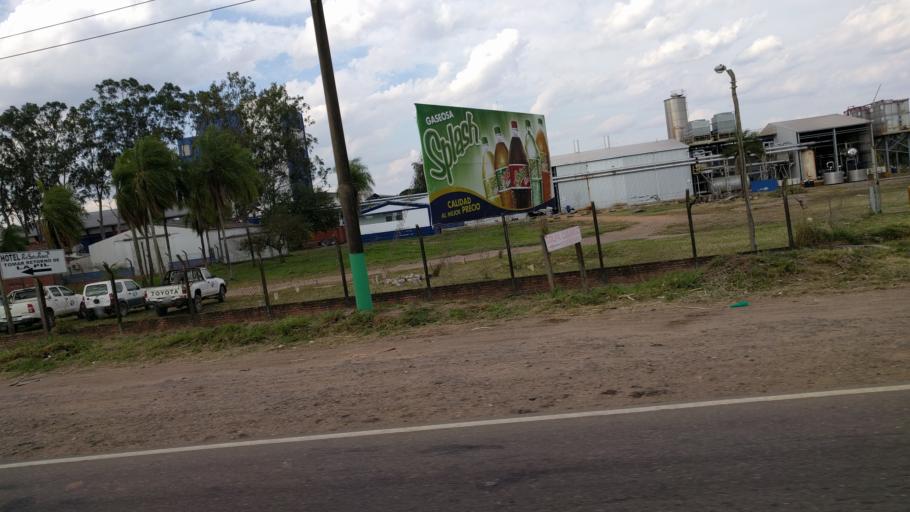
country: BO
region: Santa Cruz
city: Warnes
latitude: -17.5328
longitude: -63.1613
